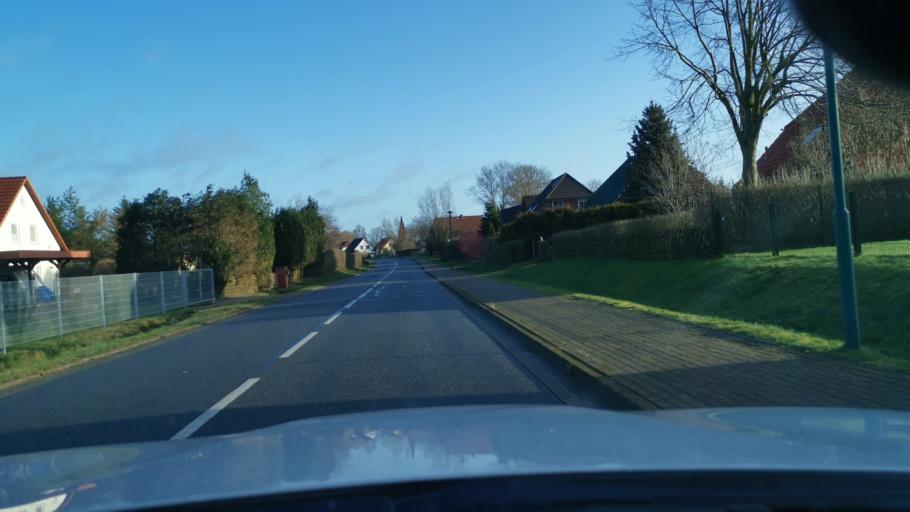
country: DE
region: Mecklenburg-Vorpommern
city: Laage
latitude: 53.9845
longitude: 12.3543
